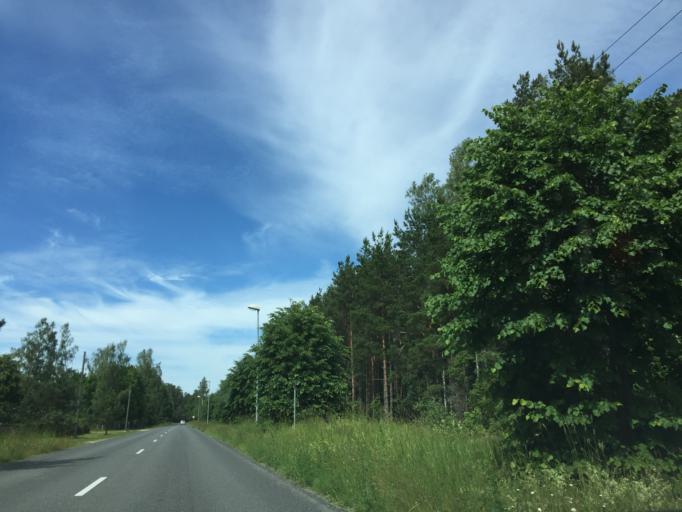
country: LV
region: Dundaga
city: Dundaga
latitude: 57.6567
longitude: 22.5720
